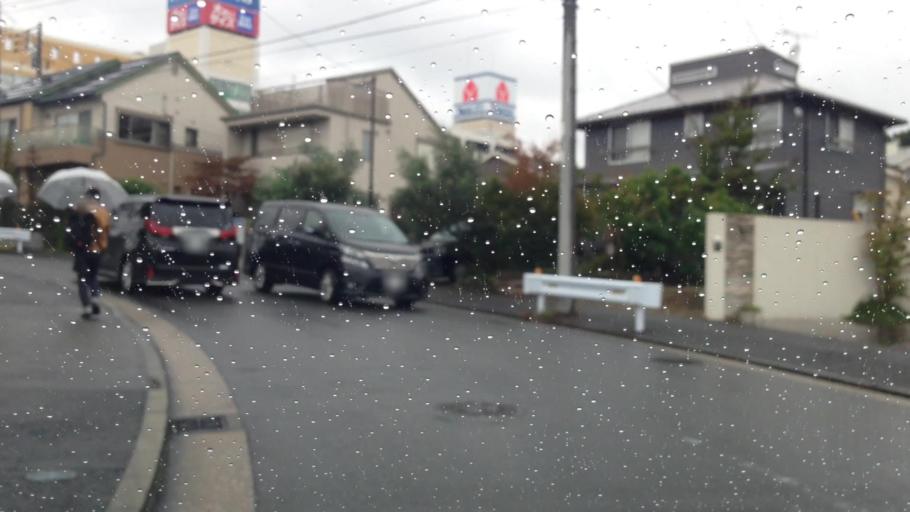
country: JP
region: Tokyo
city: Chofugaoka
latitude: 35.5476
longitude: 139.5790
